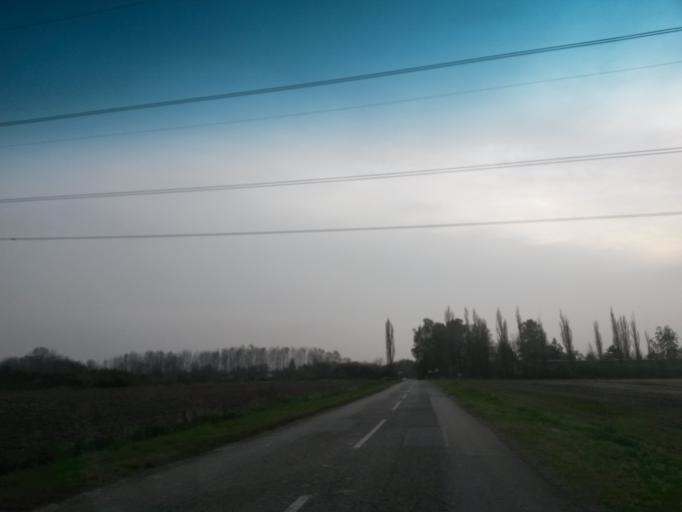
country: HR
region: Vukovarsko-Srijemska
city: Bobota
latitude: 45.3813
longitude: 18.8535
